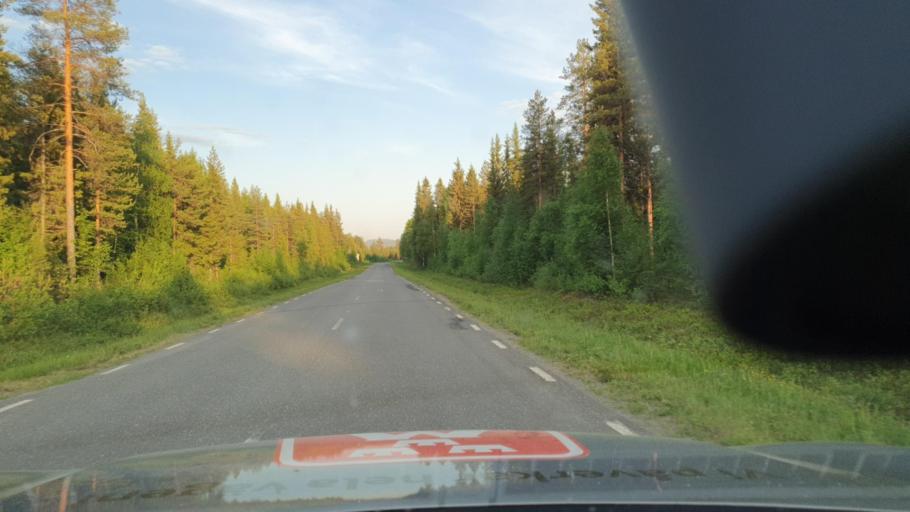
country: SE
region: Norrbotten
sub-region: Bodens Kommun
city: Boden
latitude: 66.2587
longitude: 21.3444
